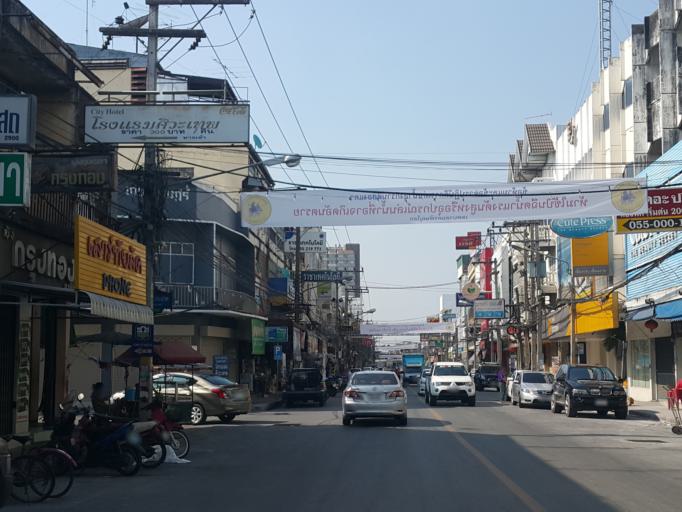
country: TH
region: Phitsanulok
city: Phitsanulok
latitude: 16.8176
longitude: 100.2650
